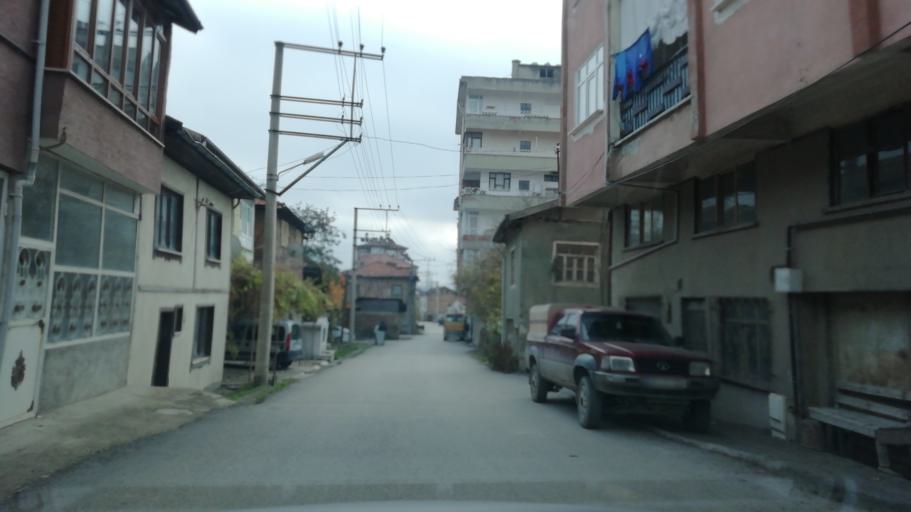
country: TR
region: Karabuk
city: Karabuk
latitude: 41.2212
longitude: 32.6274
